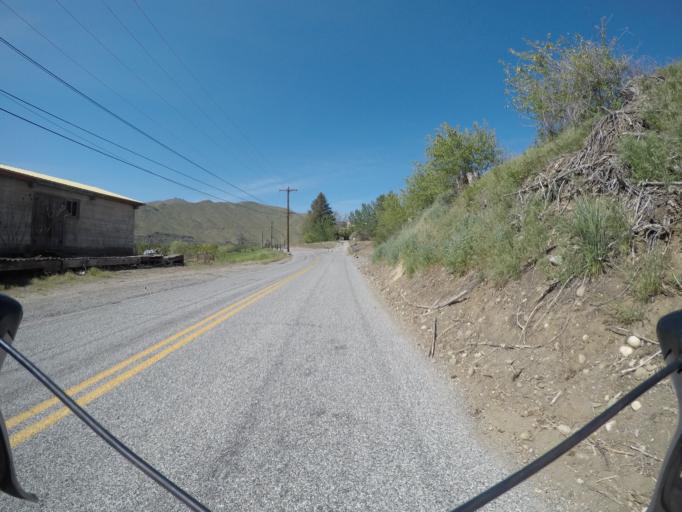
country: US
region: Washington
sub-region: Chelan County
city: Sunnyslope
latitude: 47.4709
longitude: -120.3596
